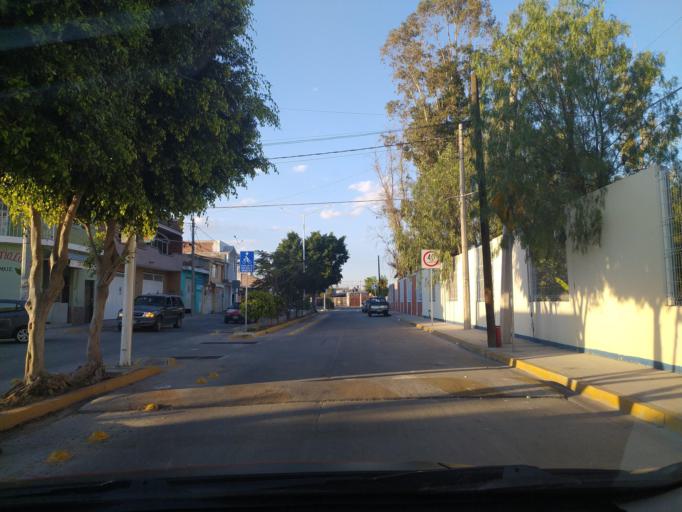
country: MX
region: Guanajuato
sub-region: San Francisco del Rincon
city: Fraccionamiento la Mezquitera
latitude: 21.0115
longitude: -101.8409
